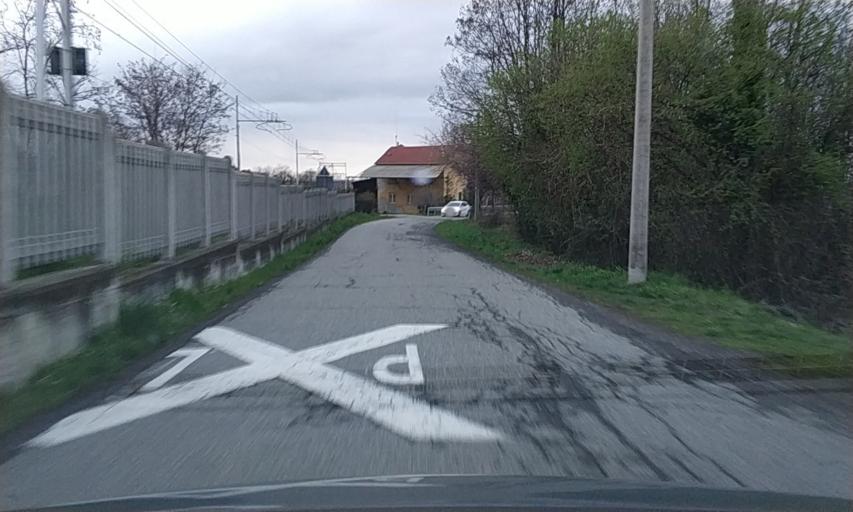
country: IT
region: Piedmont
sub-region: Provincia di Torino
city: Nole
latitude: 45.2401
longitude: 7.5753
